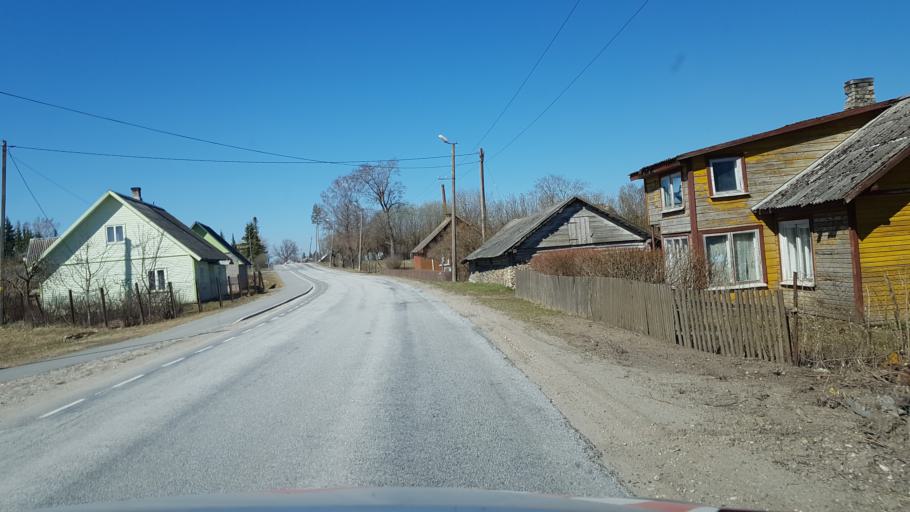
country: EE
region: Laeaene-Virumaa
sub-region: Rakke vald
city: Rakke
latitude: 58.9850
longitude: 26.2519
